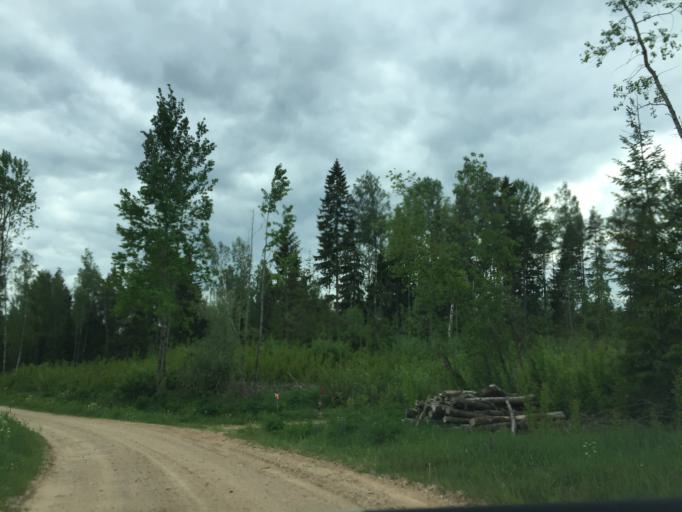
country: LV
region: Aglona
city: Aglona
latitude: 56.1787
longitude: 27.2509
